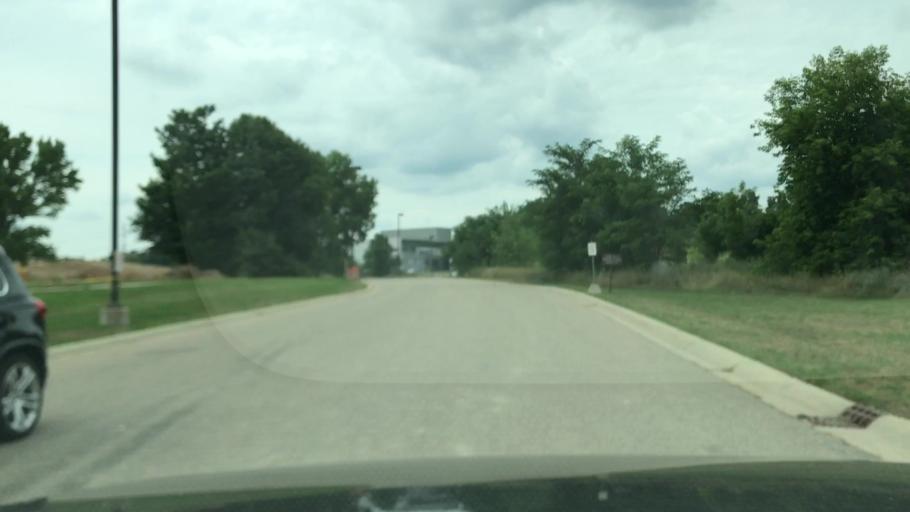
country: US
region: Michigan
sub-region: Kent County
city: East Grand Rapids
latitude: 42.9484
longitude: -85.5522
